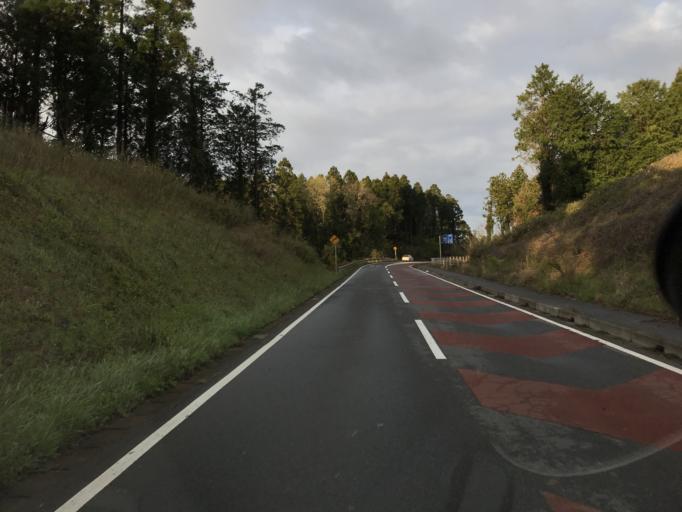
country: JP
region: Chiba
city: Yokaichiba
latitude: 35.7597
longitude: 140.4583
